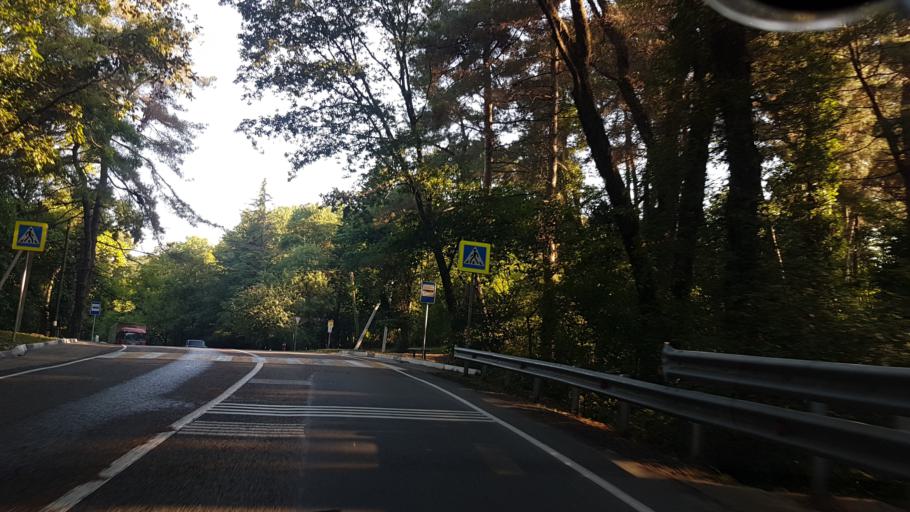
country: RU
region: Krasnodarskiy
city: Gornoye Loo
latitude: 43.6732
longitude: 39.6177
